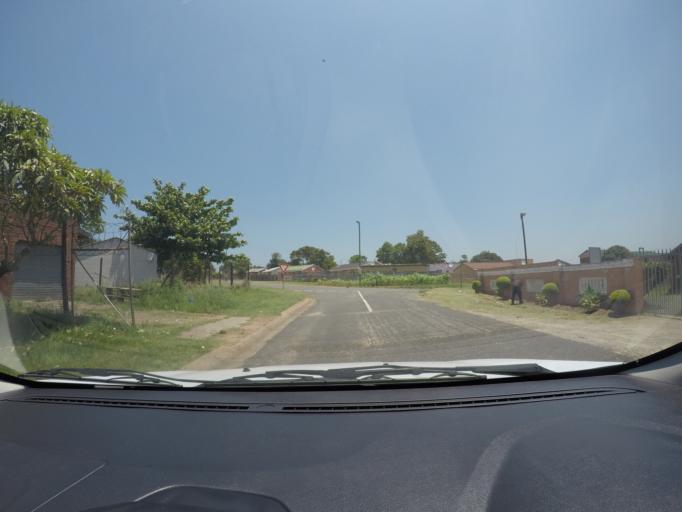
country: ZA
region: KwaZulu-Natal
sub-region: uThungulu District Municipality
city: eSikhawini
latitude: -28.8831
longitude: 31.8913
